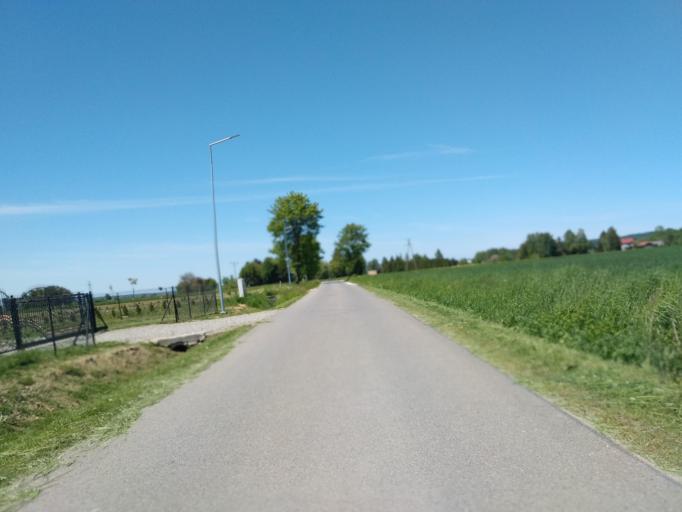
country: PL
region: Subcarpathian Voivodeship
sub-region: Powiat sanocki
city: Dlugie
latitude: 49.5952
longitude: 22.0466
